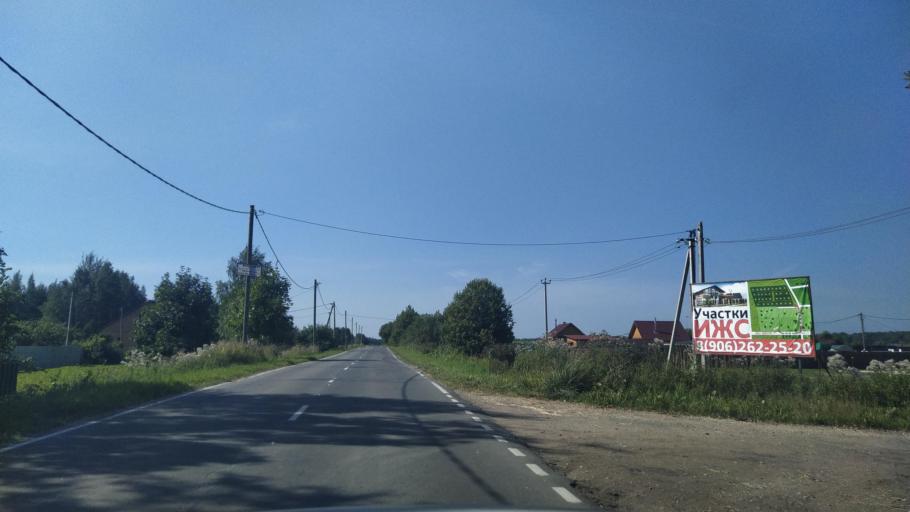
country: RU
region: Leningrad
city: Siverskiy
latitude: 59.2889
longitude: 30.0610
